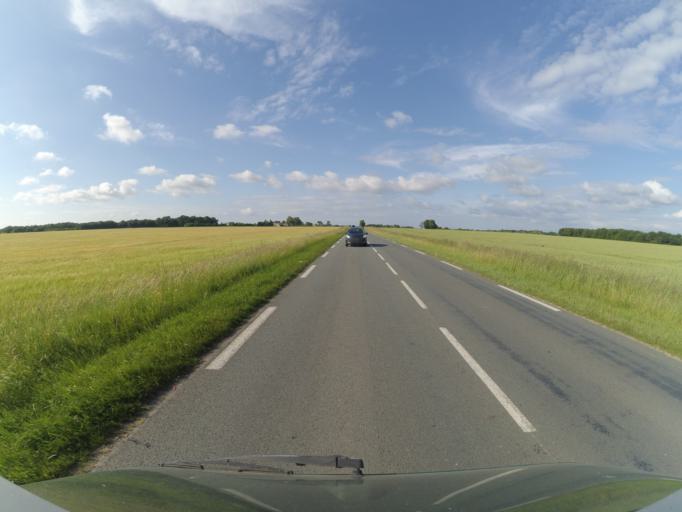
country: FR
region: Poitou-Charentes
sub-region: Departement de la Charente-Maritime
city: Le Gua
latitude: 45.7404
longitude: -0.9498
